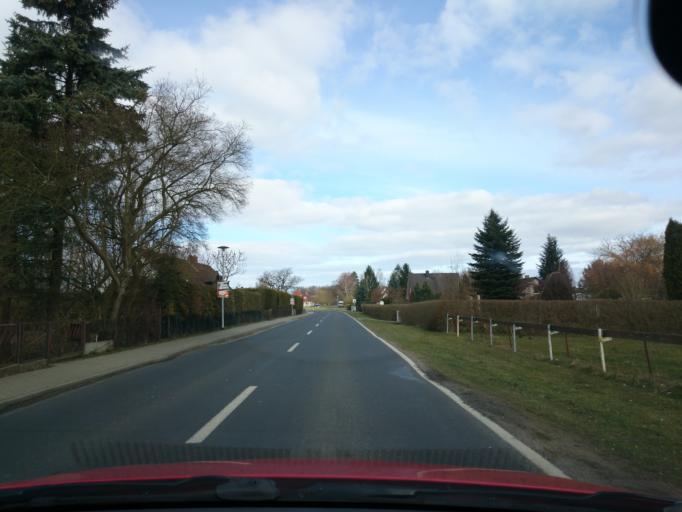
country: DE
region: Mecklenburg-Vorpommern
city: Velgast
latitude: 54.3046
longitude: 12.7924
